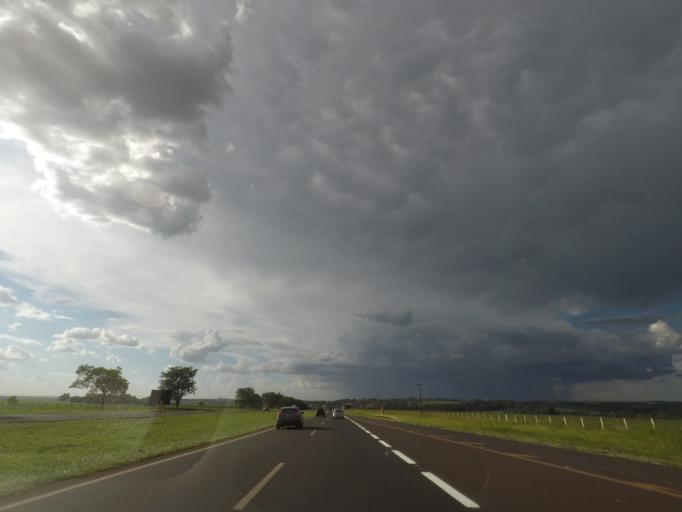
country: BR
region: Sao Paulo
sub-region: Jardinopolis
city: Jardinopolis
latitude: -21.0801
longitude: -47.8036
